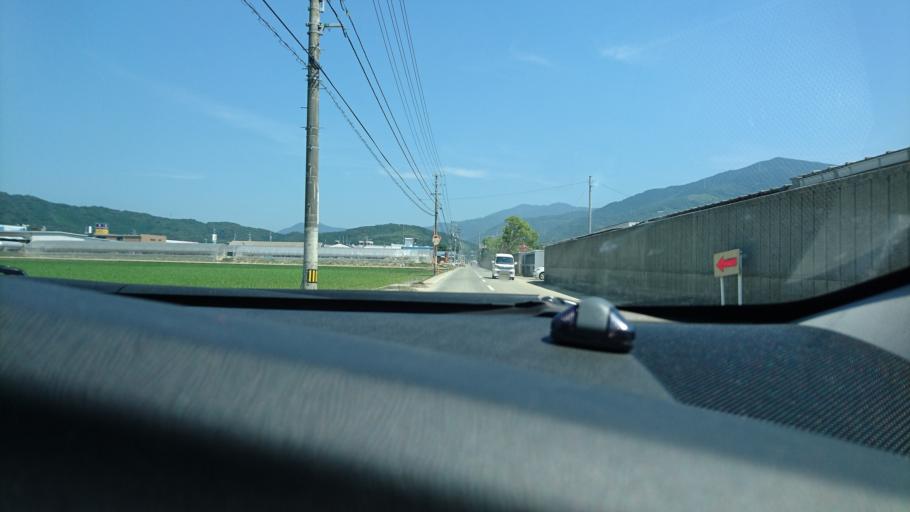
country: JP
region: Ehime
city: Ozu
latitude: 33.5262
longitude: 132.5698
